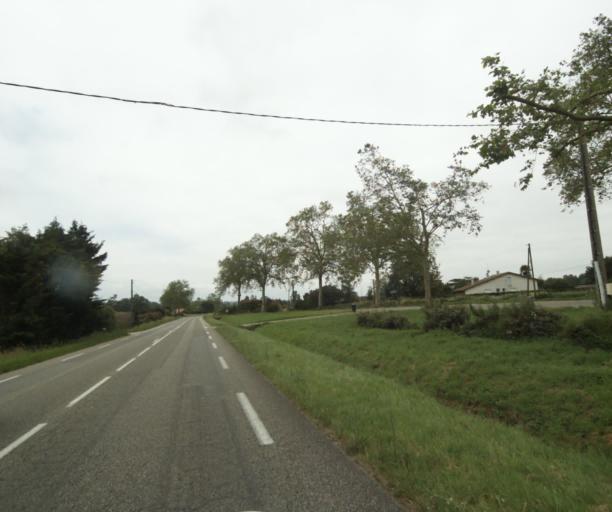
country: FR
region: Midi-Pyrenees
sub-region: Departement du Tarn-et-Garonne
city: Saint-Nauphary
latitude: 43.9747
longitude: 1.4127
